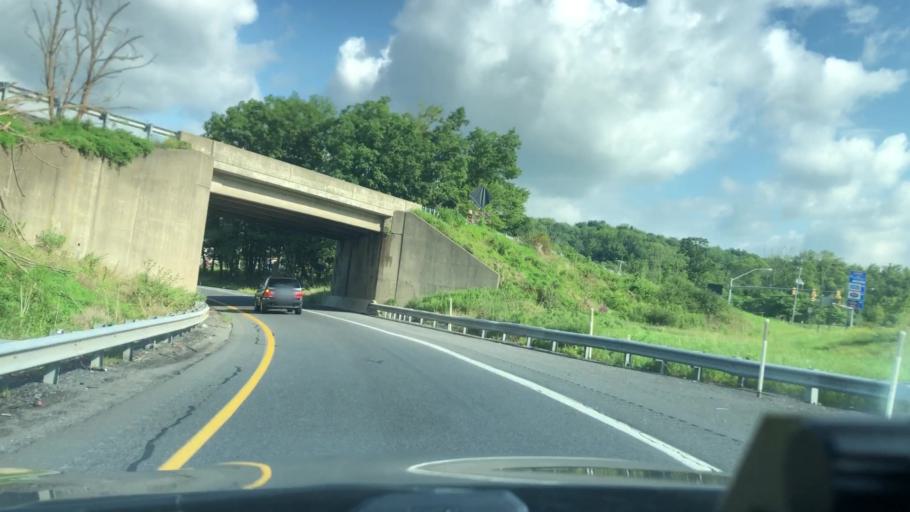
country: US
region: Pennsylvania
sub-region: Monroe County
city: Arlington Heights
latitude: 40.9989
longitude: -75.2694
